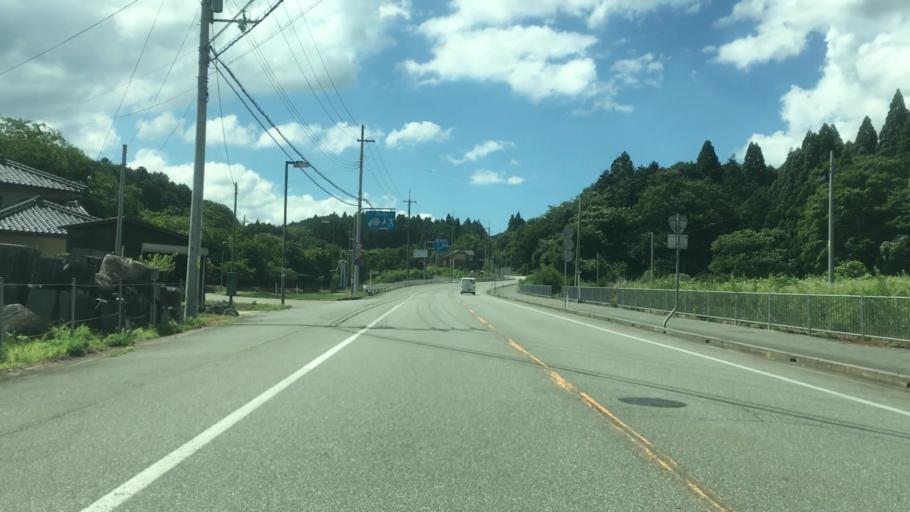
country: JP
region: Hyogo
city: Toyooka
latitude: 35.4840
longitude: 134.7061
